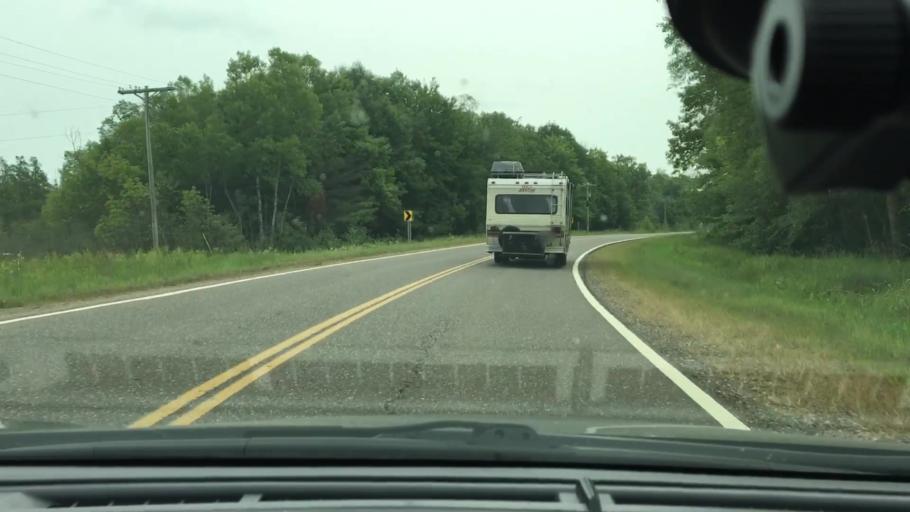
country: US
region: Minnesota
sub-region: Aitkin County
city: Aitkin
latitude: 46.4066
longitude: -93.8087
